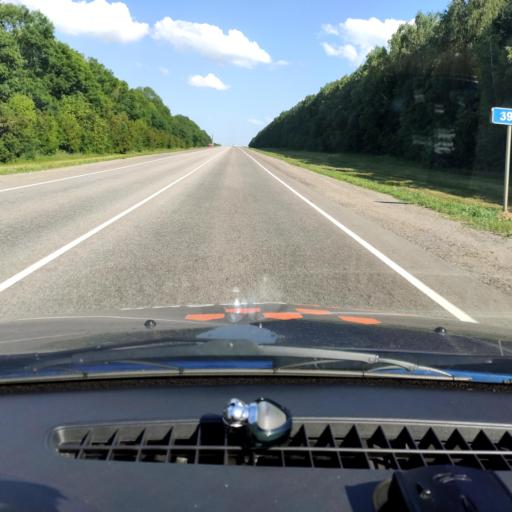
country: RU
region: Lipetsk
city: Yelets
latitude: 52.5700
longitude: 38.6628
